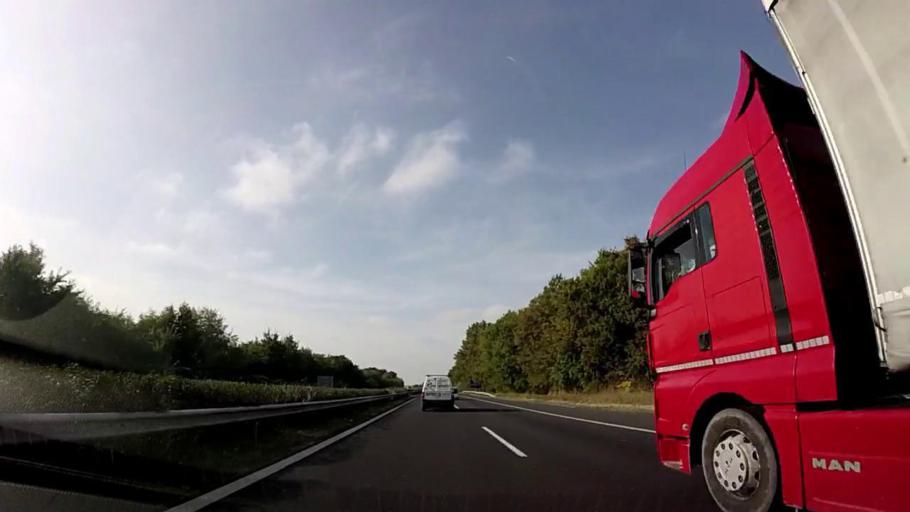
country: HU
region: Fejer
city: Lepseny
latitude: 47.0295
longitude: 18.2669
